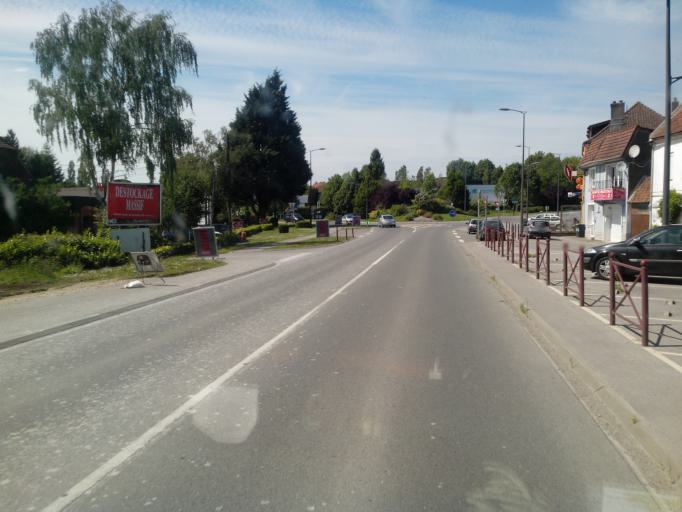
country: FR
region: Nord-Pas-de-Calais
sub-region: Departement du Pas-de-Calais
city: Montreuil
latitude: 50.4807
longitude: 1.7647
